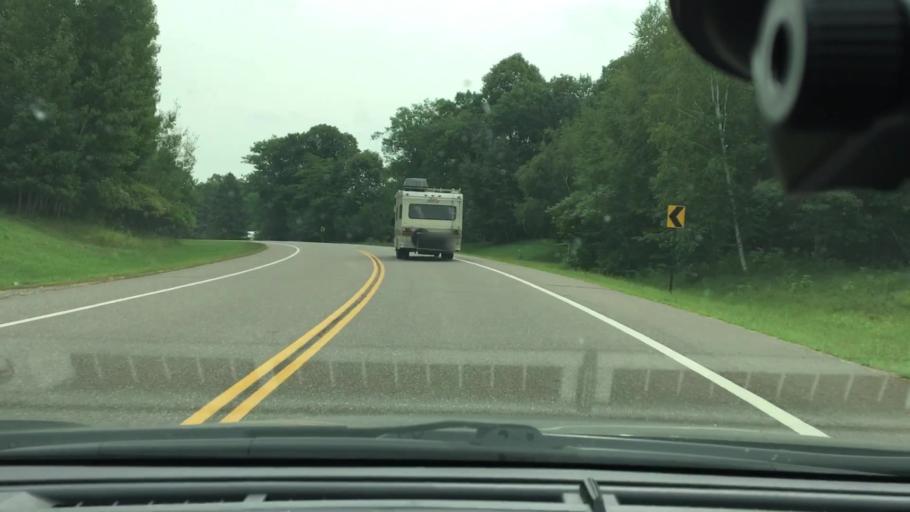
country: US
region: Minnesota
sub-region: Crow Wing County
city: Crosby
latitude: 46.4085
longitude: -93.8225
